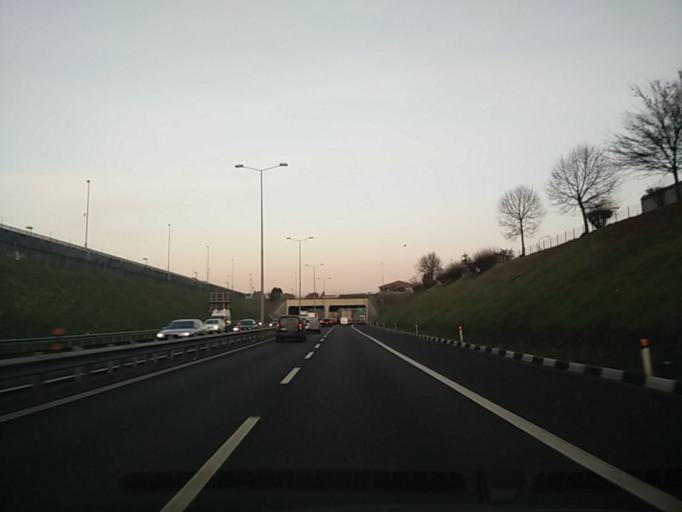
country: IT
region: Lombardy
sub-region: Citta metropolitana di Milano
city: Cinisello Balsamo
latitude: 45.5644
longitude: 9.2342
